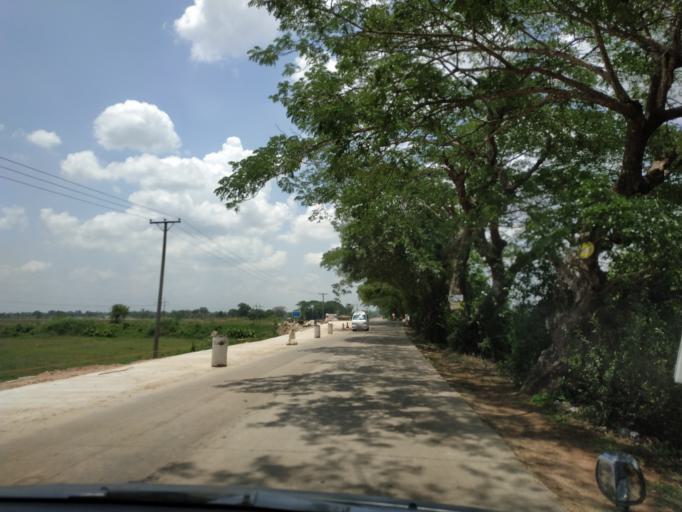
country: MM
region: Bago
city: Bago
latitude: 17.4788
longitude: 96.4947
